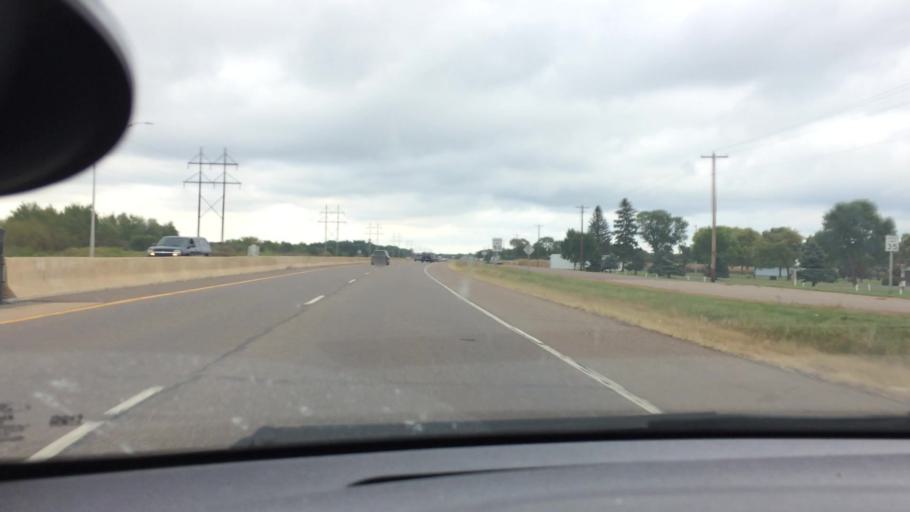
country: US
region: Wisconsin
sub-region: Chippewa County
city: Lake Hallie
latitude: 44.9011
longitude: -91.4134
